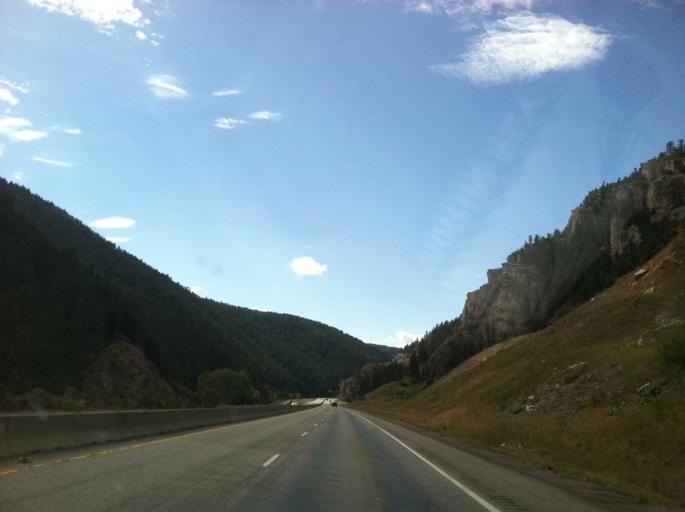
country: US
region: Montana
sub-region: Gallatin County
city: Bozeman
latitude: 45.6425
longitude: -110.9033
